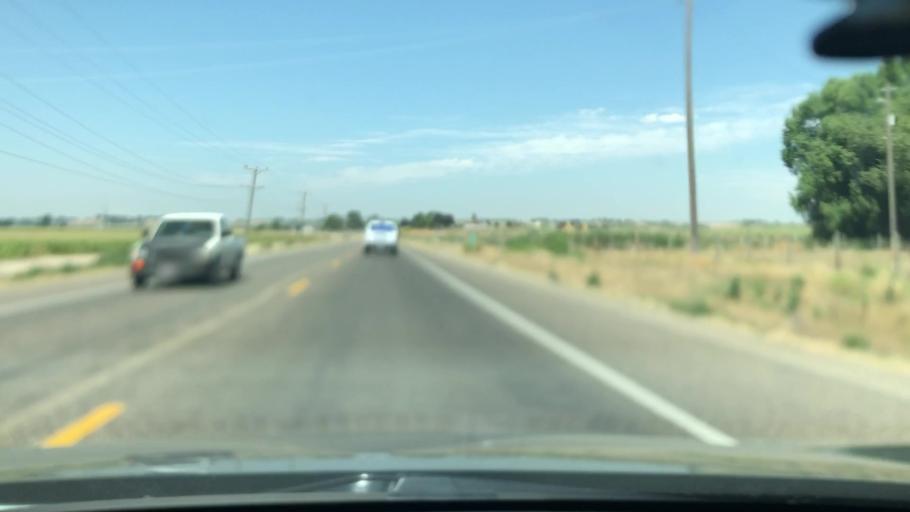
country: US
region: Idaho
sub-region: Owyhee County
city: Homedale
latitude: 43.6332
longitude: -116.9115
